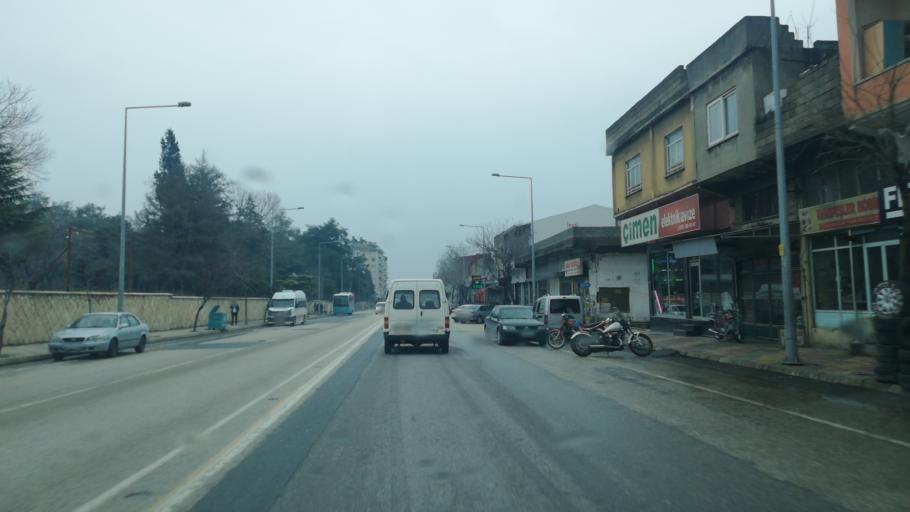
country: TR
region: Kahramanmaras
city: Kahramanmaras
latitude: 37.5741
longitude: 36.9381
